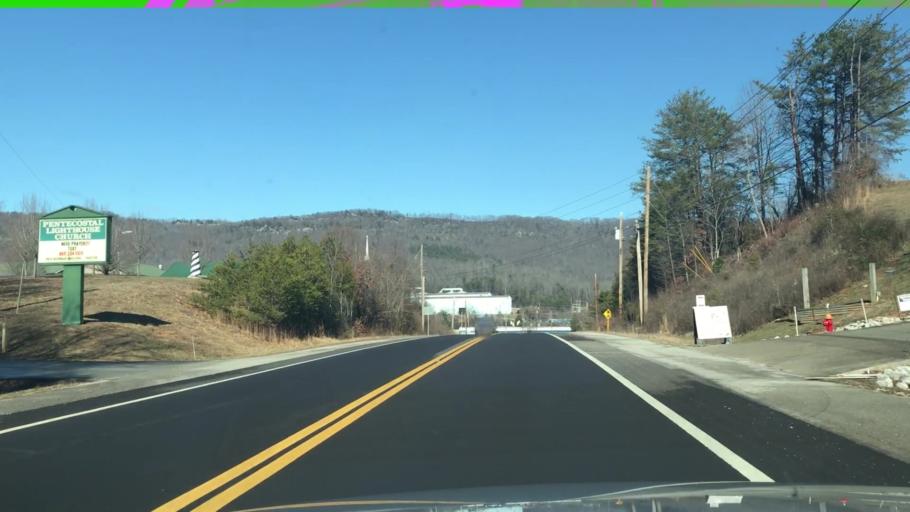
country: US
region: Tennessee
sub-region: Roane County
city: Midtown
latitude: 35.8919
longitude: -84.6179
